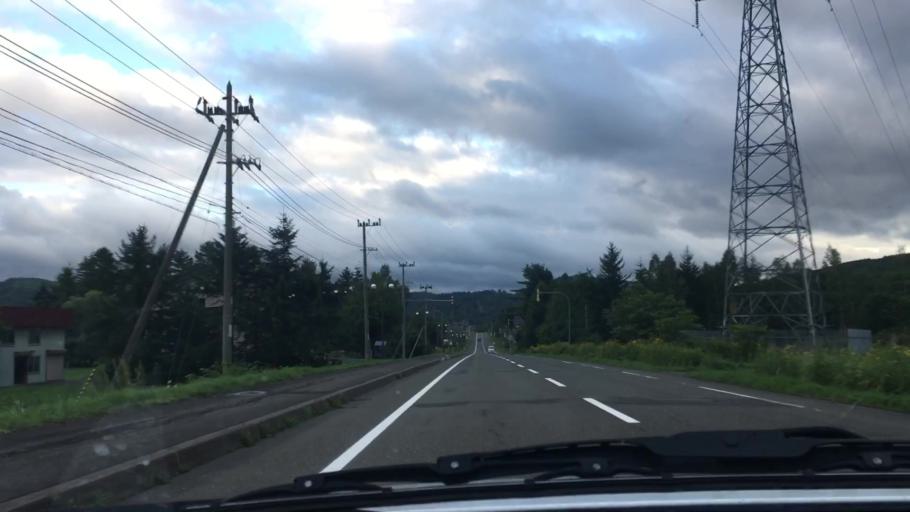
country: JP
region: Hokkaido
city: Shimo-furano
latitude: 42.9974
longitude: 142.4040
